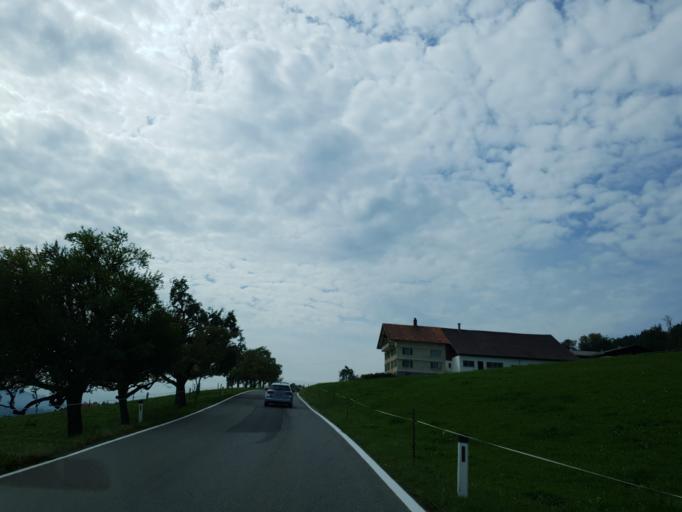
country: AT
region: Vorarlberg
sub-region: Politischer Bezirk Bregenz
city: Sulzberg
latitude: 47.4966
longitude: 9.8998
